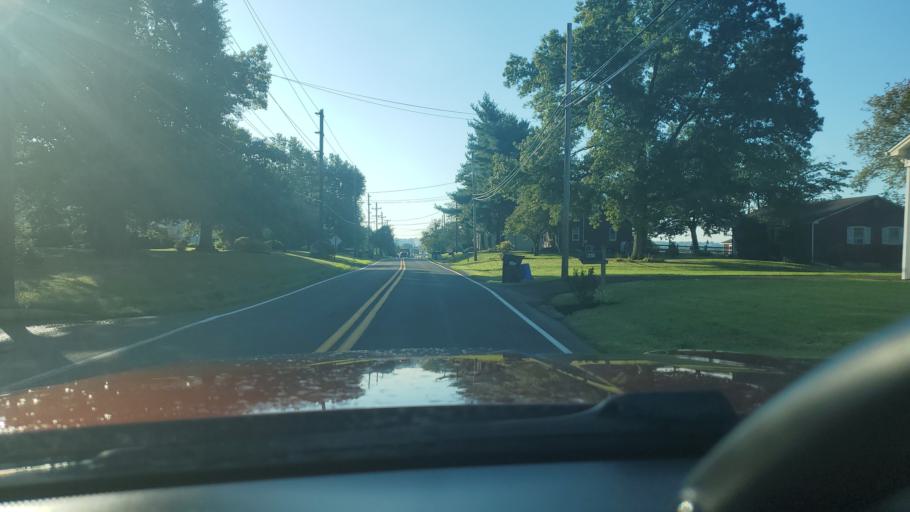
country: US
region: Pennsylvania
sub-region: Montgomery County
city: Woxall
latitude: 40.2926
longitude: -75.4303
